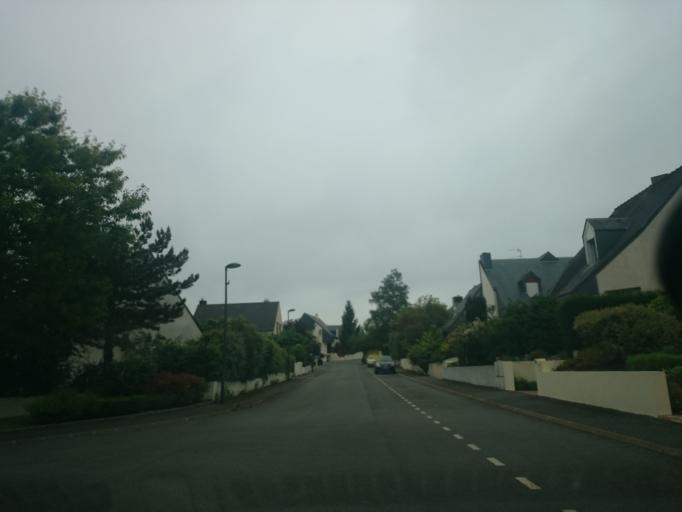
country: FR
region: Brittany
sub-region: Departement d'Ille-et-Vilaine
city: Cesson-Sevigne
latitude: 48.1285
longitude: -1.6008
